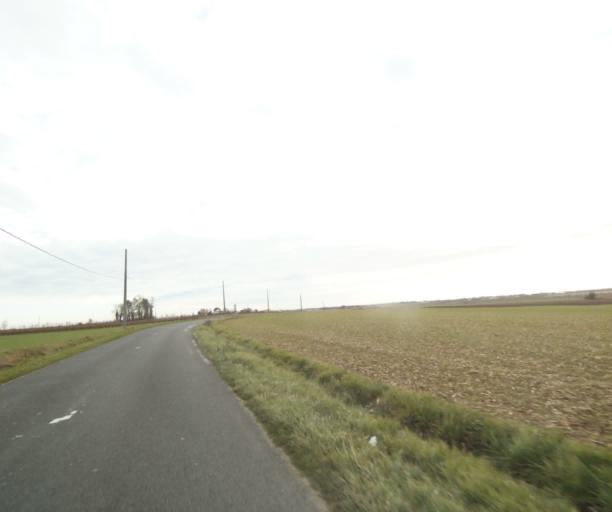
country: FR
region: Poitou-Charentes
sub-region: Departement de la Charente-Maritime
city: Corme-Royal
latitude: 45.7379
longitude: -0.8142
